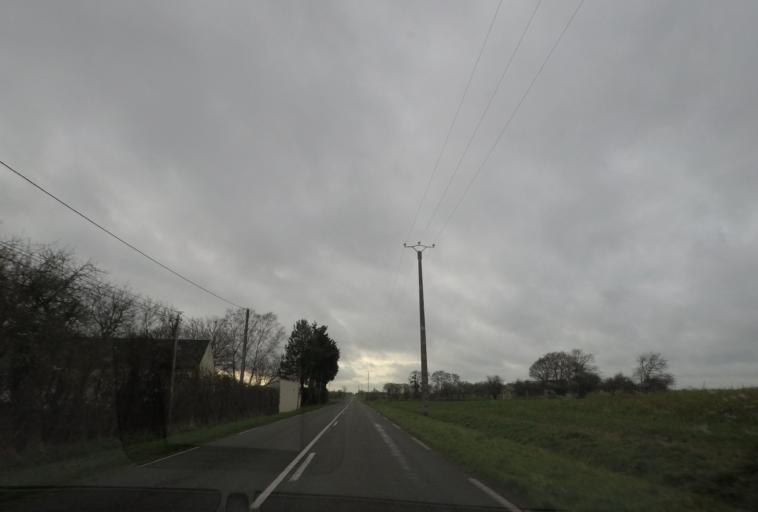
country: FR
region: Pays de la Loire
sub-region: Departement de la Sarthe
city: Saint-Calais
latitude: 47.9775
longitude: 0.7605
